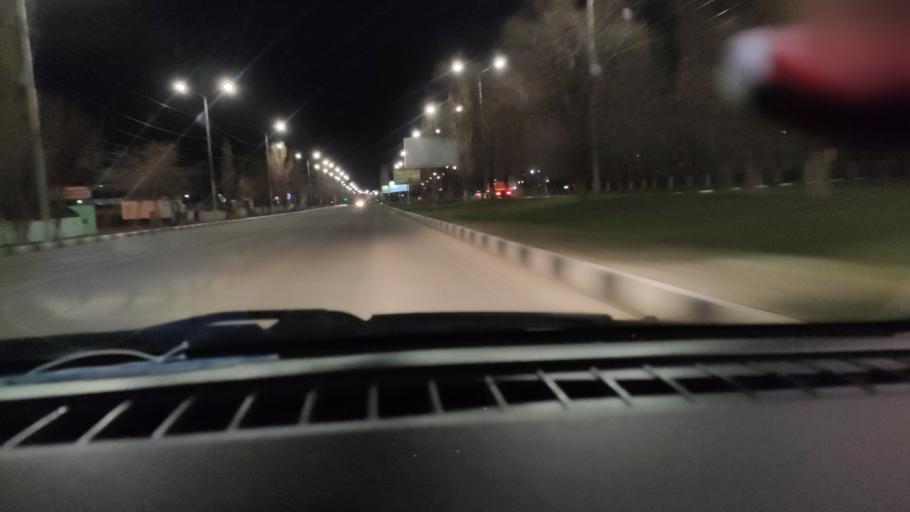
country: RU
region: Saratov
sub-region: Saratovskiy Rayon
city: Saratov
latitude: 51.6063
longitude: 45.9695
